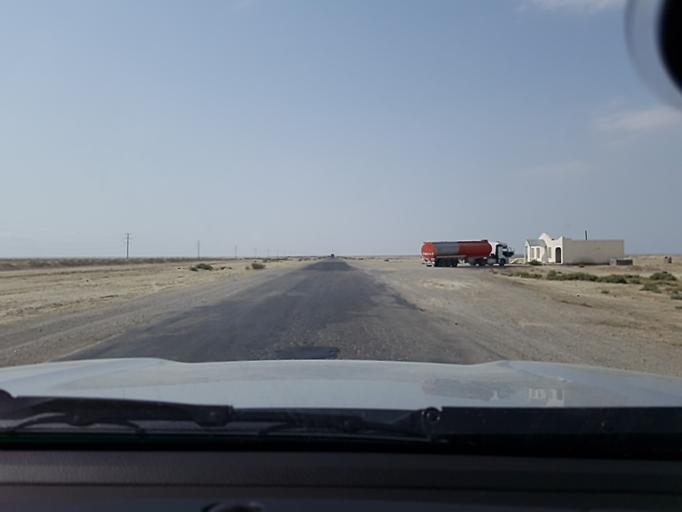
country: TM
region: Balkan
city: Gumdag
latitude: 38.9968
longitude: 54.5864
